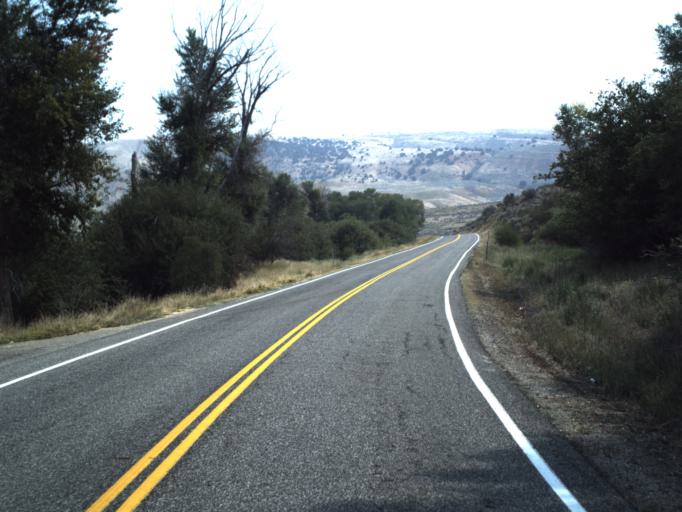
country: US
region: Utah
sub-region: Morgan County
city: Morgan
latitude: 40.9856
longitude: -111.5359
